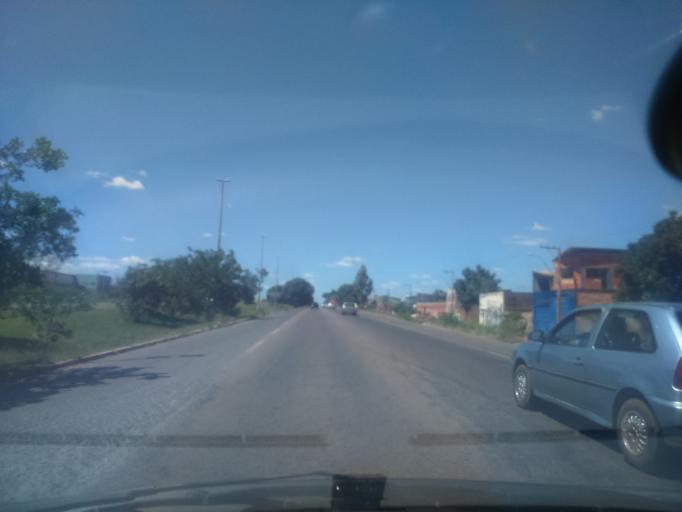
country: BR
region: Goias
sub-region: Luziania
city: Luziania
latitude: -16.0492
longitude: -47.9970
